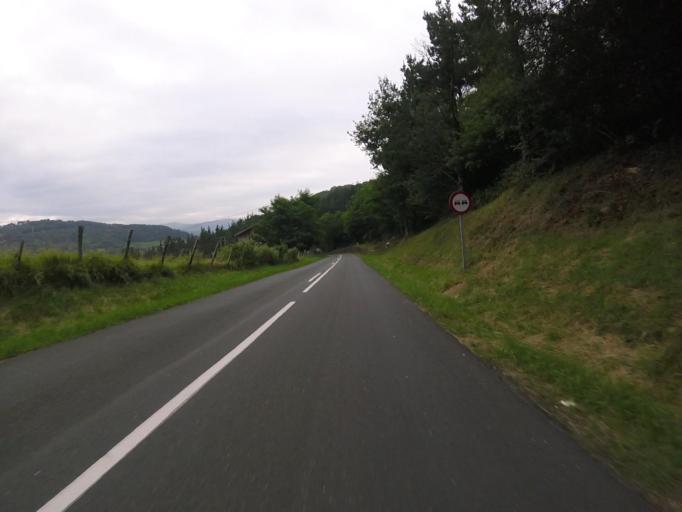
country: ES
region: Basque Country
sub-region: Provincia de Guipuzcoa
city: Lezo
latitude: 43.3133
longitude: -1.8496
